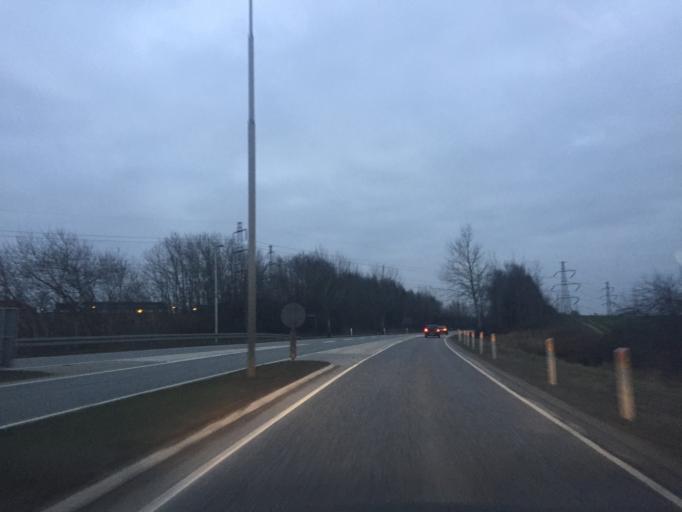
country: DK
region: Capital Region
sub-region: Frederikssund Kommune
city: Slangerup
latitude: 55.8470
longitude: 12.1509
